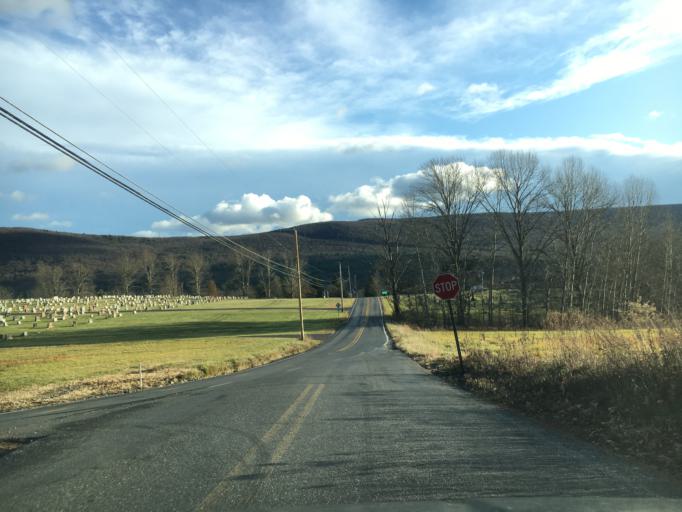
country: US
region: Pennsylvania
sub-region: Carbon County
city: Lehighton
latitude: 40.7890
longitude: -75.7158
